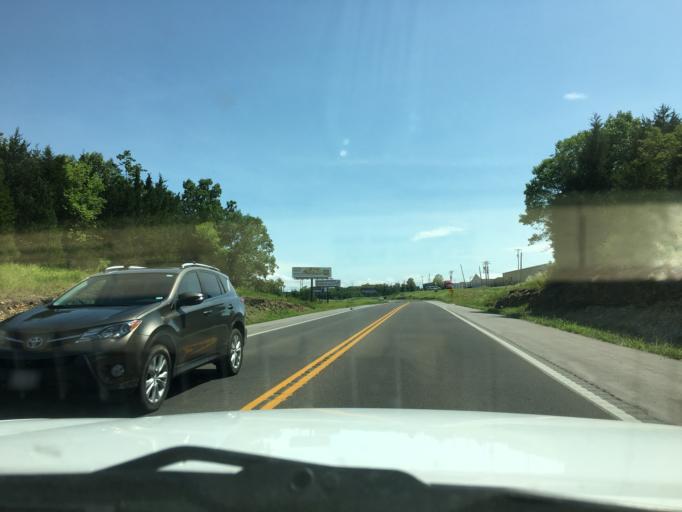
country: US
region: Missouri
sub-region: Franklin County
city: Union
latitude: 38.4932
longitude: -91.0042
